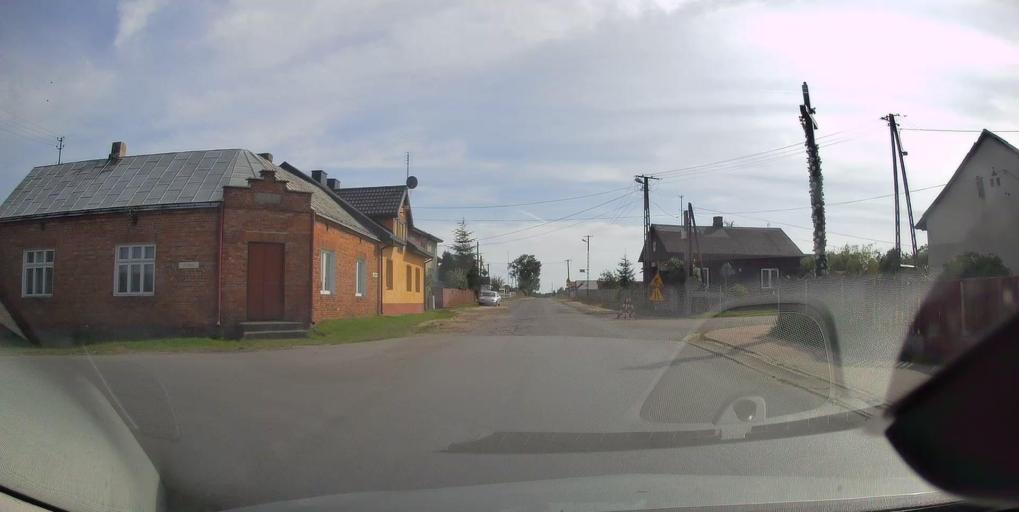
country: PL
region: Lodz Voivodeship
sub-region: Powiat tomaszowski
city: Tomaszow Mazowiecki
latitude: 51.4552
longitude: 20.0353
